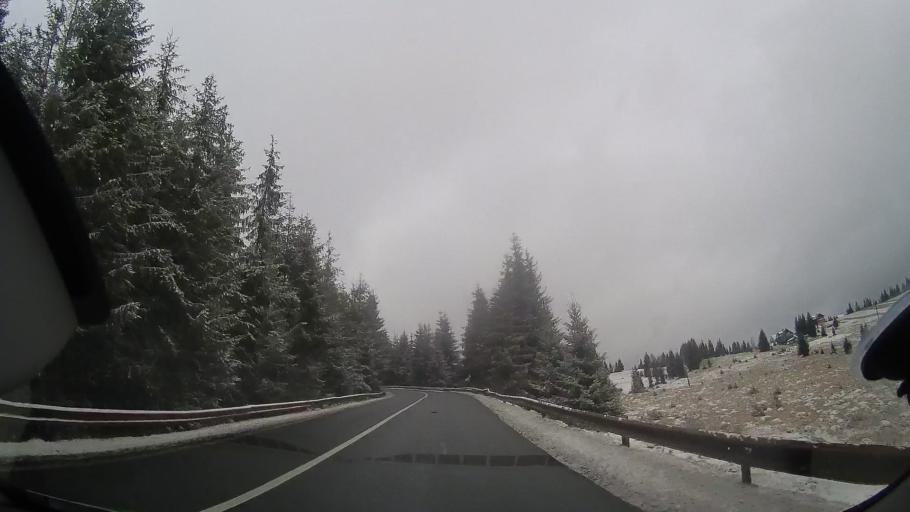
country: RO
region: Cluj
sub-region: Comuna Belis
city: Belis
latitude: 46.6773
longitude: 23.0447
